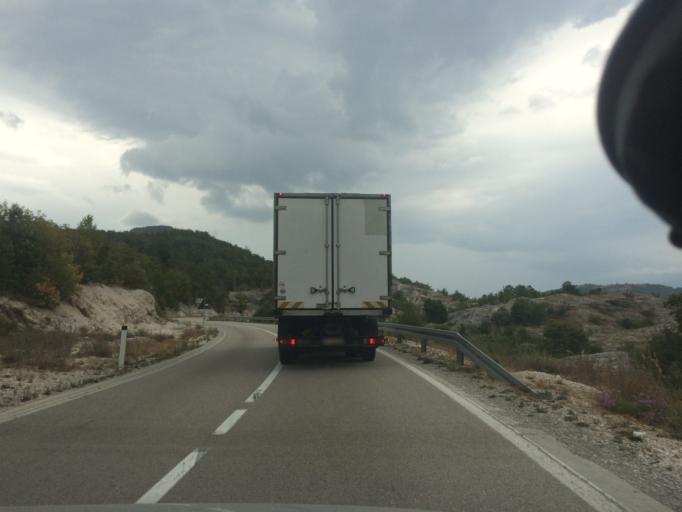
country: ME
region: Kotor
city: Risan
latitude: 42.6968
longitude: 18.6316
